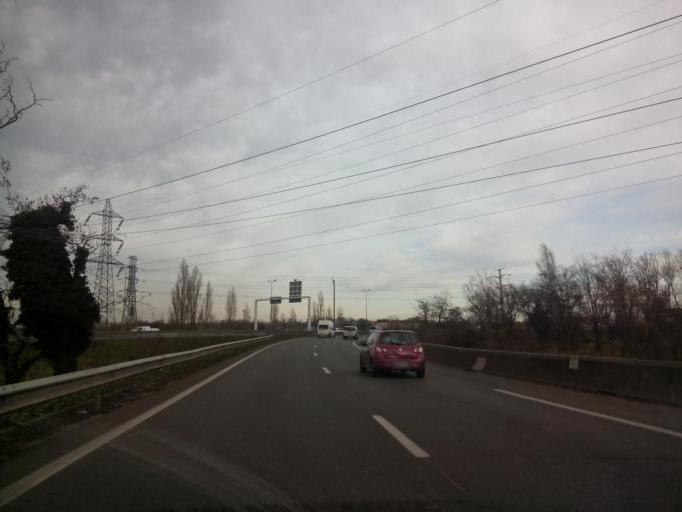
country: FR
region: Rhone-Alpes
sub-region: Departement du Rhone
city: Saint-Fons
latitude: 45.7146
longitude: 4.8439
